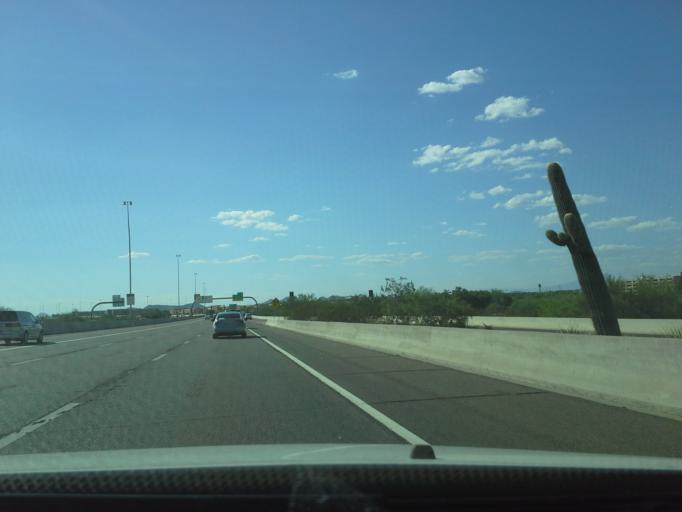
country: US
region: Arizona
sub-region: Maricopa County
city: Paradise Valley
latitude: 33.6692
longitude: -111.9625
